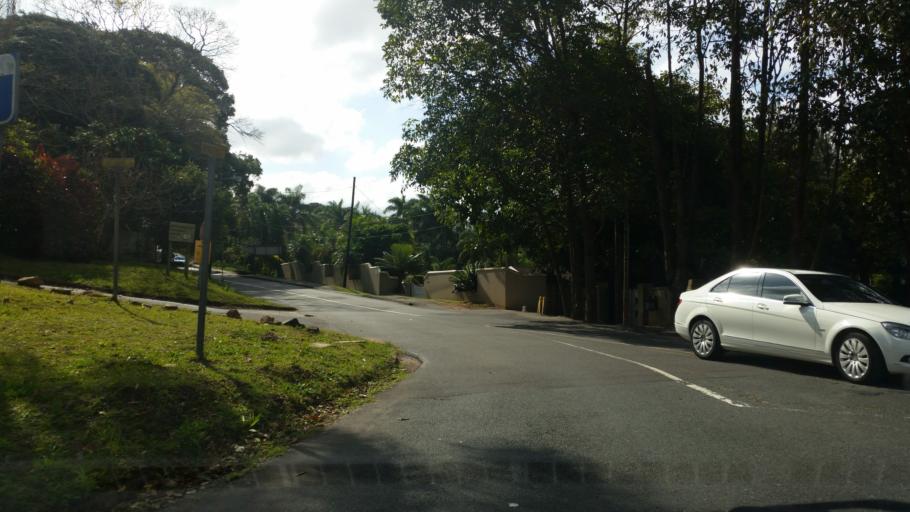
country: ZA
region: KwaZulu-Natal
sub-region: eThekwini Metropolitan Municipality
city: Berea
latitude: -29.8357
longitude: 30.9020
